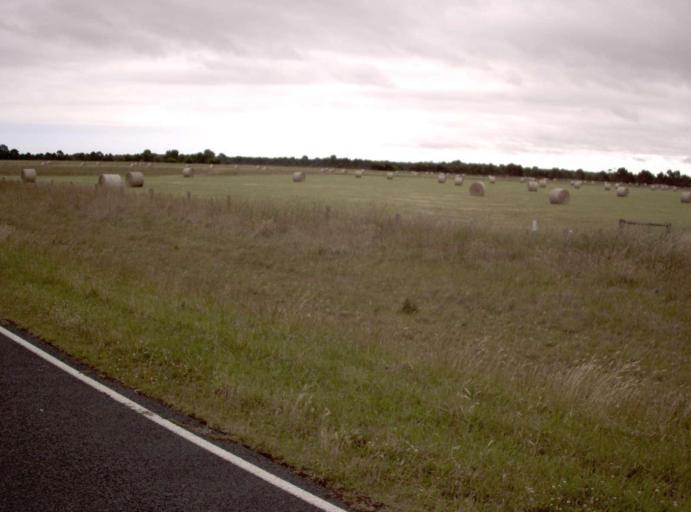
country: AU
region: Victoria
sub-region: Wellington
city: Sale
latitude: -38.5647
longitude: 146.8796
